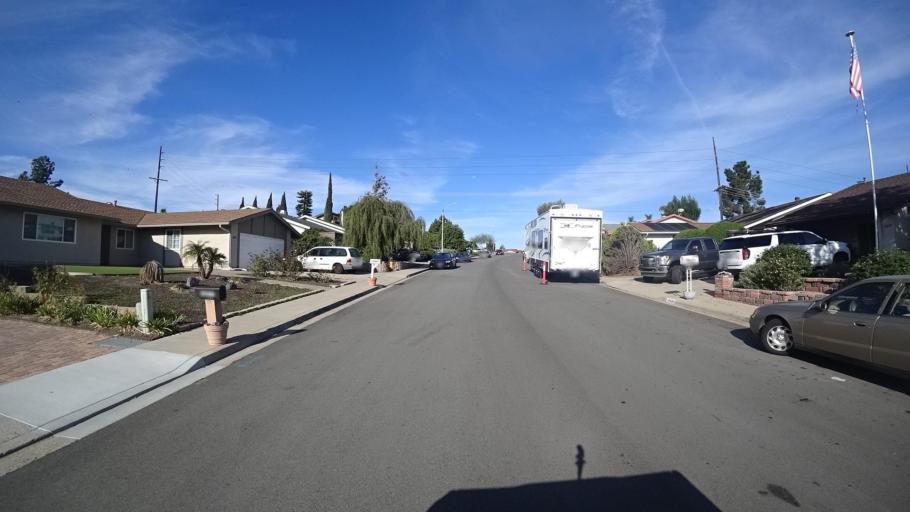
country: US
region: California
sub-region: San Diego County
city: Casa de Oro-Mount Helix
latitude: 32.7409
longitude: -116.9596
